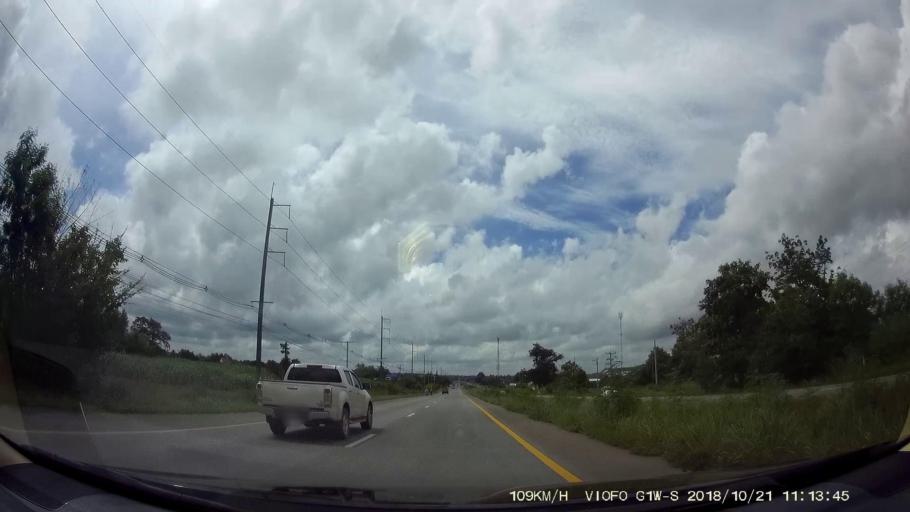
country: TH
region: Chaiyaphum
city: Chaiyaphum
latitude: 15.9125
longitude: 102.1296
